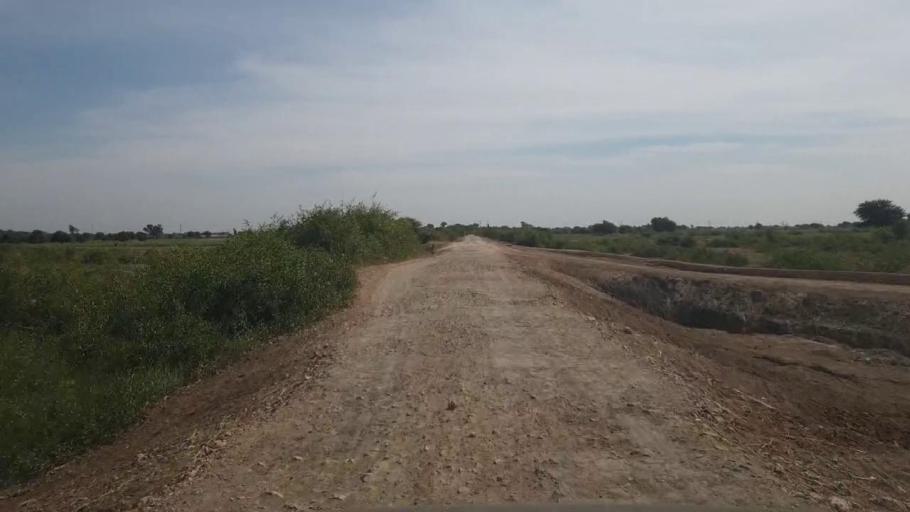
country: PK
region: Sindh
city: Kunri
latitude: 25.2881
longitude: 69.5905
